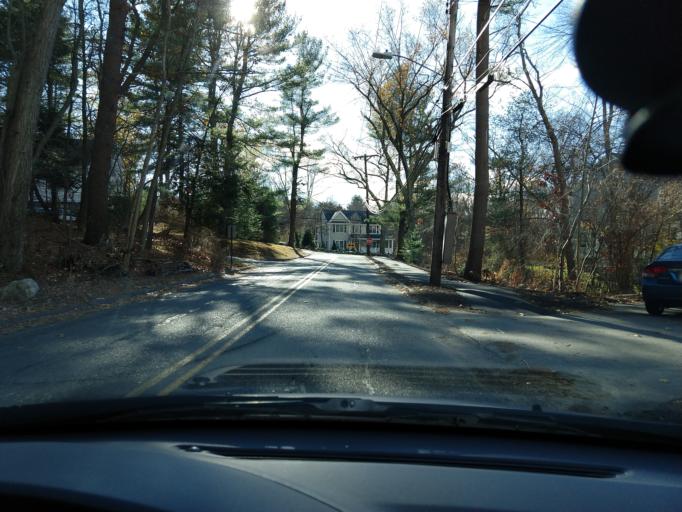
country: US
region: Massachusetts
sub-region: Middlesex County
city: Bedford
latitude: 42.4939
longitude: -71.2540
